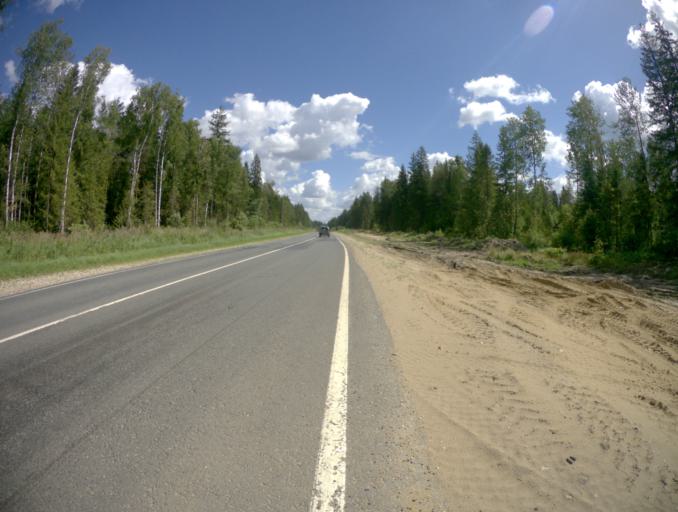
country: RU
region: Vladimir
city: Orgtrud
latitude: 56.0109
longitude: 40.6080
